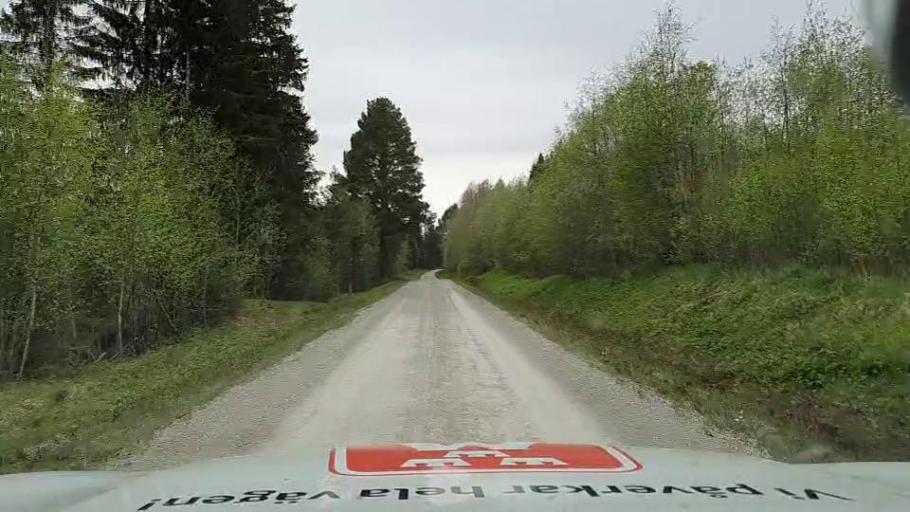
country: SE
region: Jaemtland
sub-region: Bergs Kommun
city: Hoverberg
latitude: 62.6687
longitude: 14.8134
